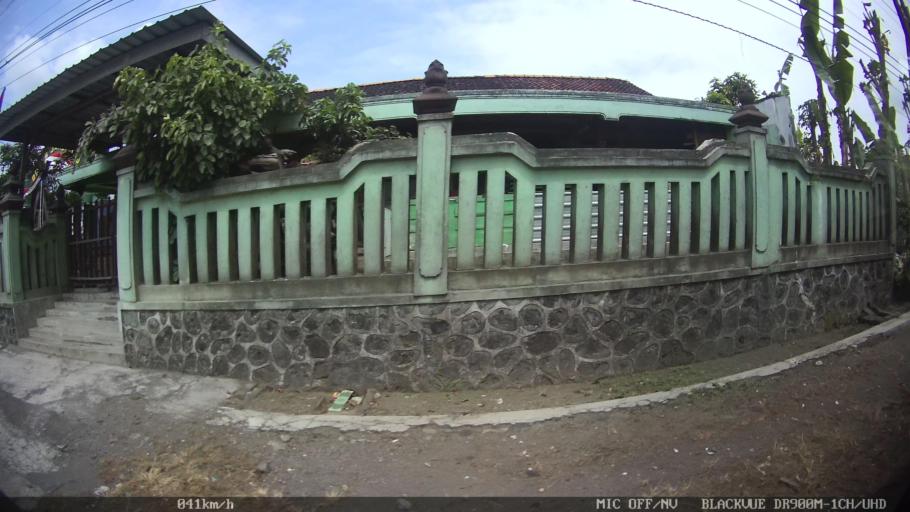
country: ID
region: Central Java
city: Candi Prambanan
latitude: -7.7309
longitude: 110.4626
